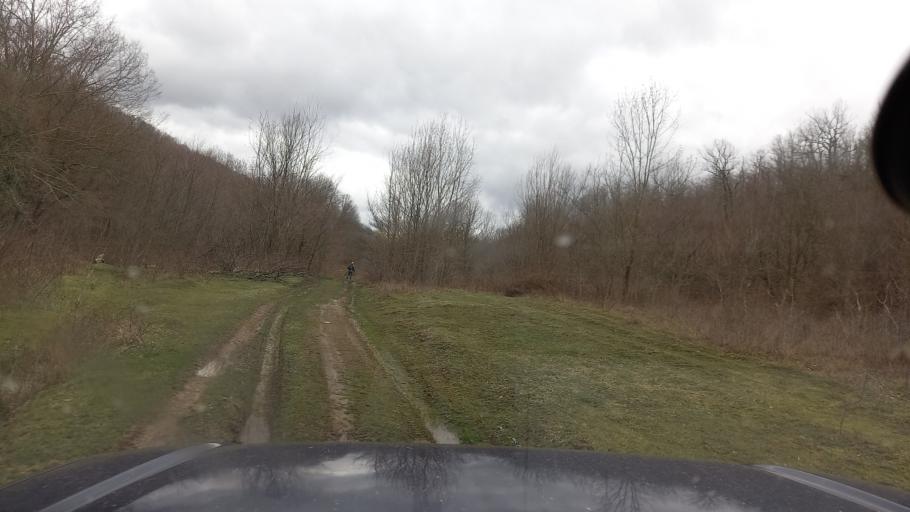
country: RU
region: Krasnodarskiy
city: Pshada
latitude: 44.4862
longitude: 38.3988
